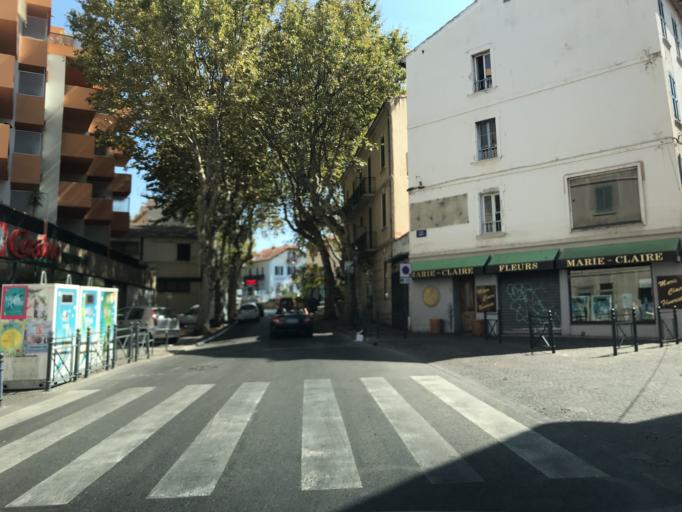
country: FR
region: Provence-Alpes-Cote d'Azur
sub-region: Departement du Var
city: La Seyne-sur-Mer
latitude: 43.1005
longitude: 5.8823
